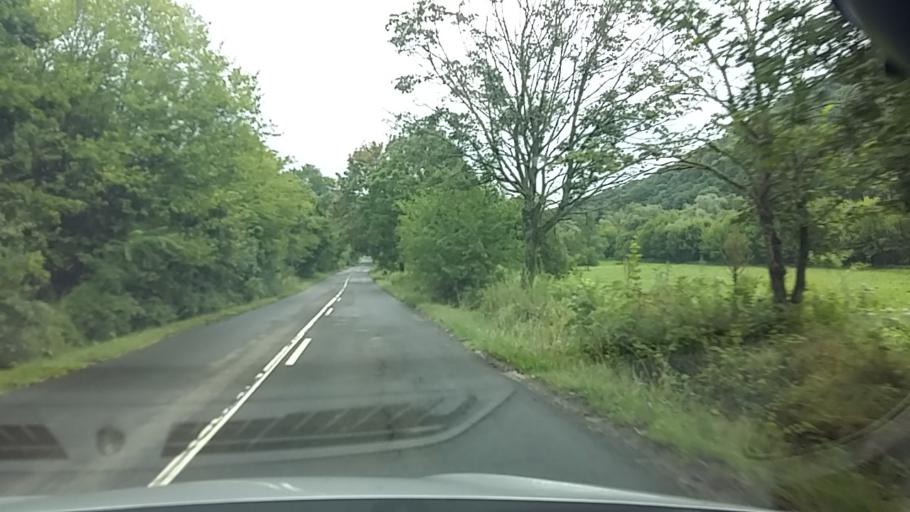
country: HU
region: Pest
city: Szob
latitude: 47.8584
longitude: 18.8024
